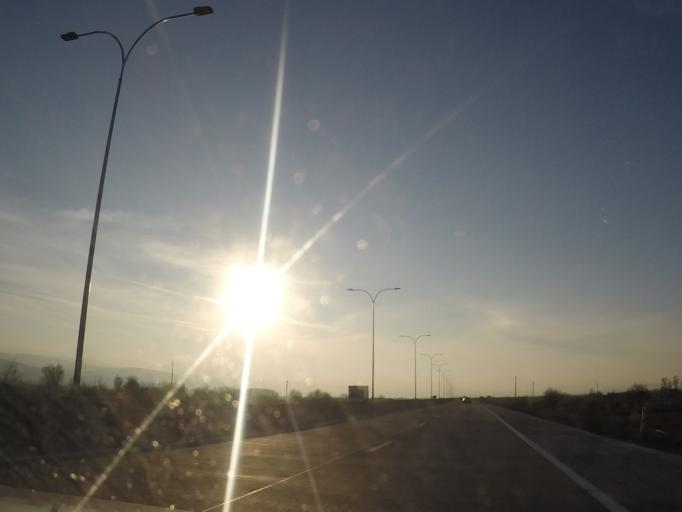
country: GE
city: Agara
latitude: 42.0284
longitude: 43.8195
